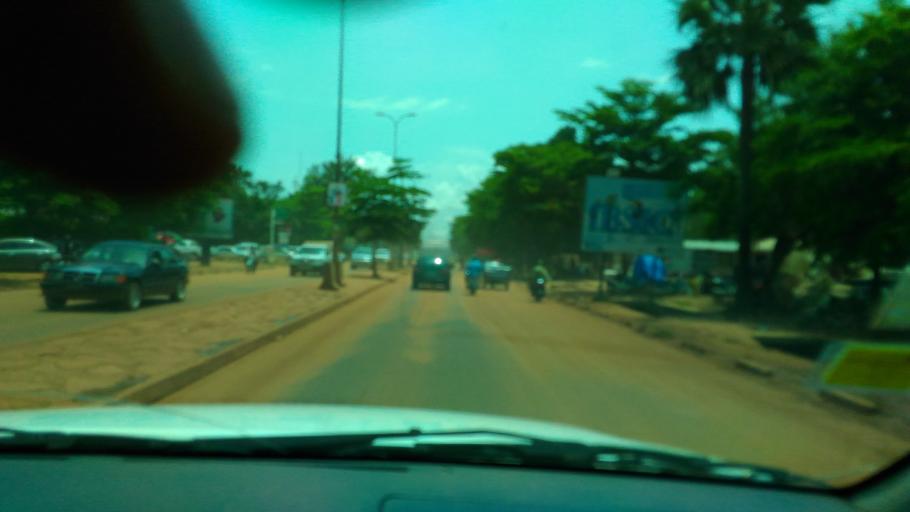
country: ML
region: Bamako
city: Bamako
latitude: 12.6557
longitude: -7.9732
